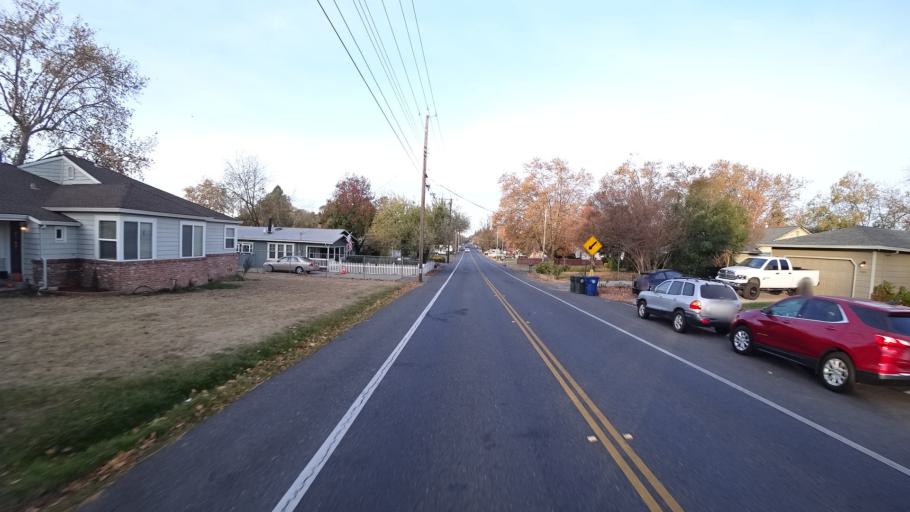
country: US
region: California
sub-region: Sacramento County
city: Citrus Heights
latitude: 38.7184
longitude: -121.2867
